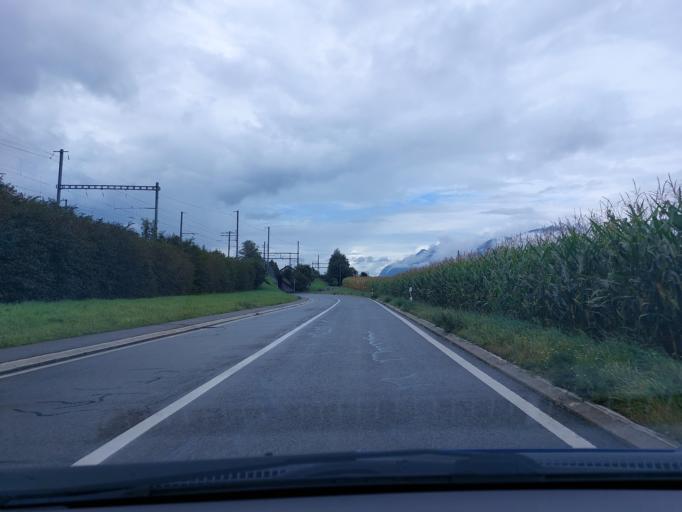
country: CH
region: Valais
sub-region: Saint-Maurice District
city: Saint-Maurice
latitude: 46.2303
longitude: 7.0002
